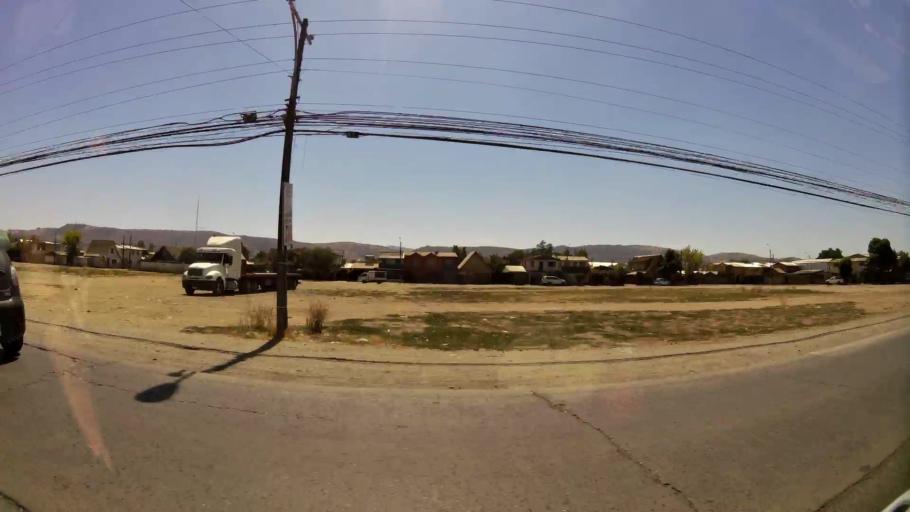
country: CL
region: Maule
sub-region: Provincia de Talca
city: Talca
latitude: -35.4115
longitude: -71.6508
